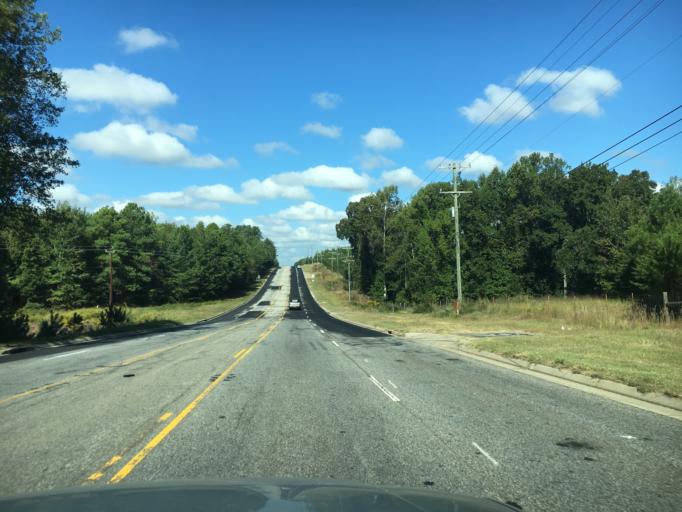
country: US
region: South Carolina
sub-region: Greenville County
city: Greer
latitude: 34.9051
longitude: -82.1944
